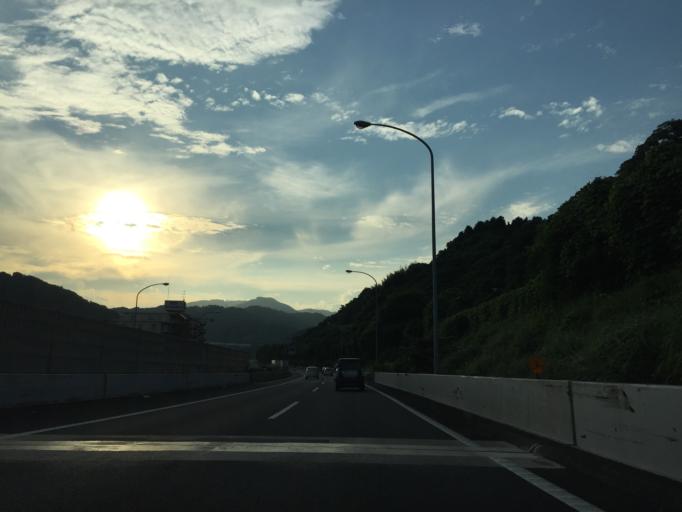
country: JP
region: Kanagawa
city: Odawara
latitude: 35.3577
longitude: 139.1102
